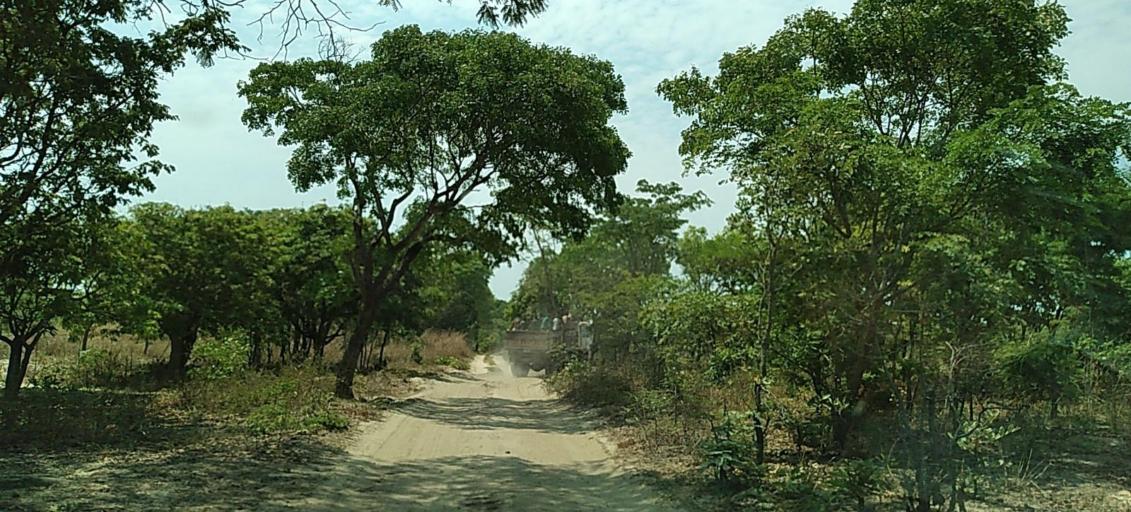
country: ZM
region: Copperbelt
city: Kalulushi
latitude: -12.9314
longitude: 28.1103
